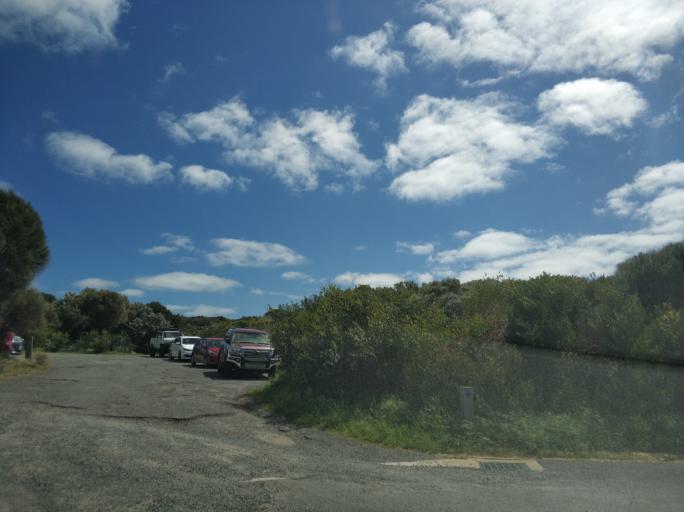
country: AU
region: Victoria
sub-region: Colac-Otway
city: Apollo Bay
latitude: -38.8539
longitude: 143.5150
